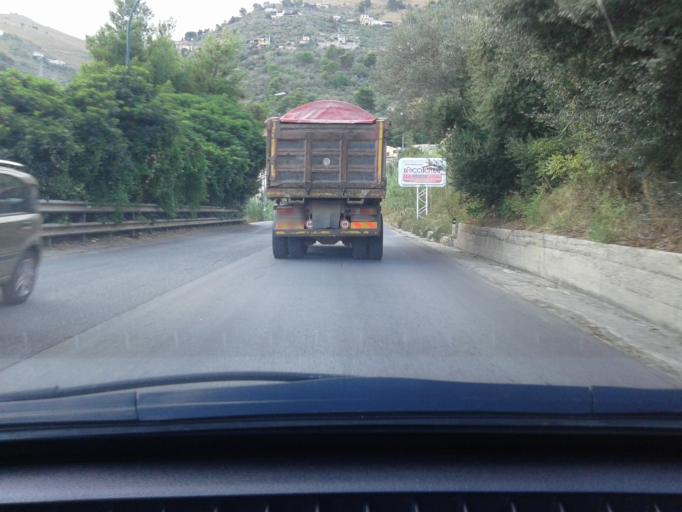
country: IT
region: Sicily
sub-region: Palermo
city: Monreale
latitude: 38.0748
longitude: 13.2830
